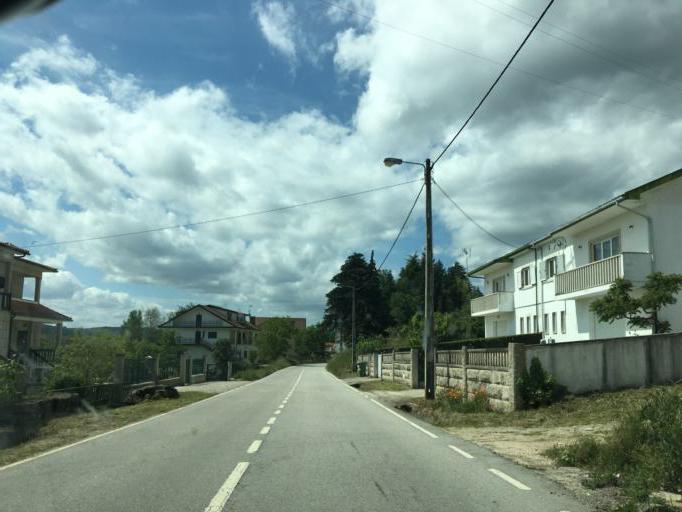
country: PT
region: Vila Real
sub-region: Boticas
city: Boticas
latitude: 41.7059
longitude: -7.6414
